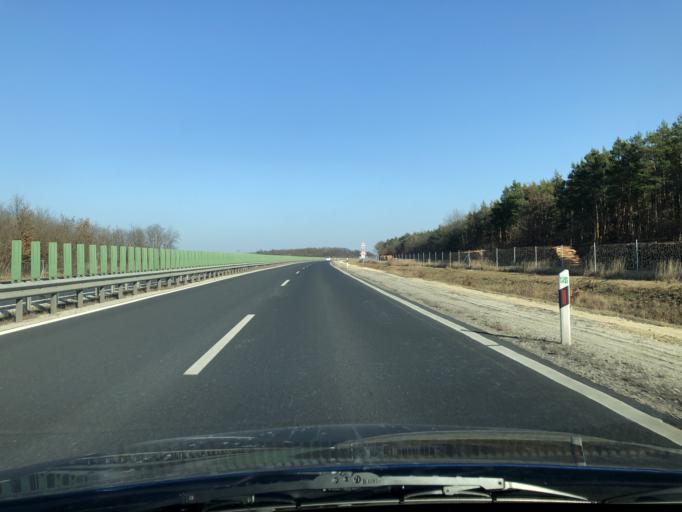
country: HU
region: Vas
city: Vep
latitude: 47.2887
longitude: 16.8157
